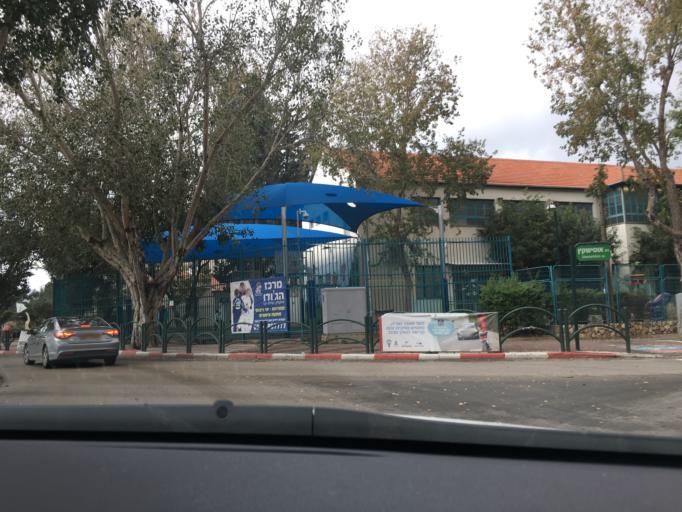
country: IL
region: Tel Aviv
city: Ramat HaSharon
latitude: 32.1444
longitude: 34.8444
